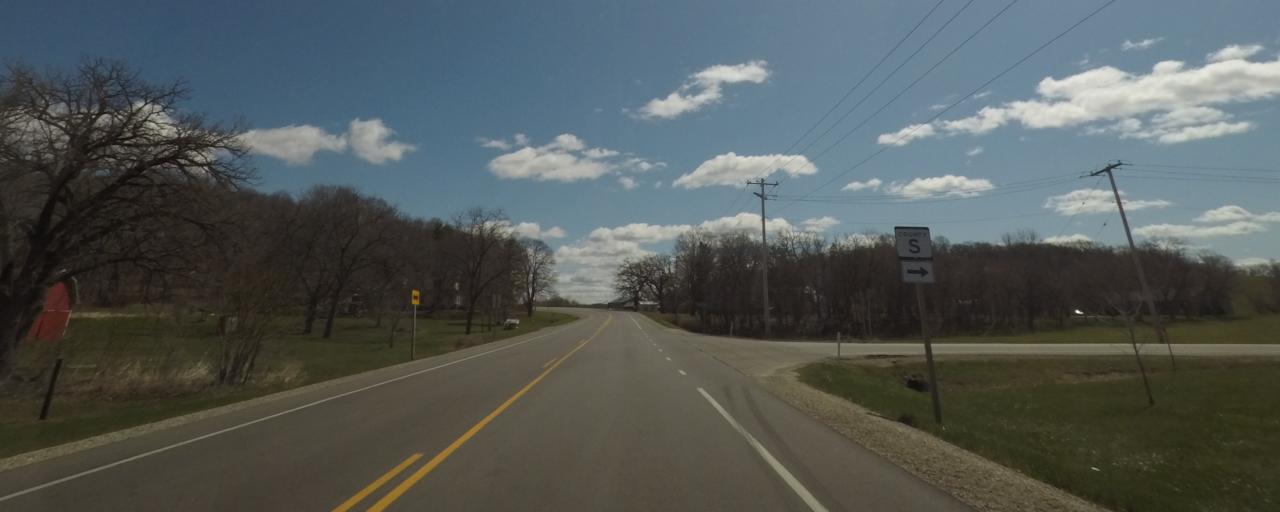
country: US
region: Wisconsin
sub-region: Jefferson County
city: Lake Mills
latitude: 43.0884
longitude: -88.9586
